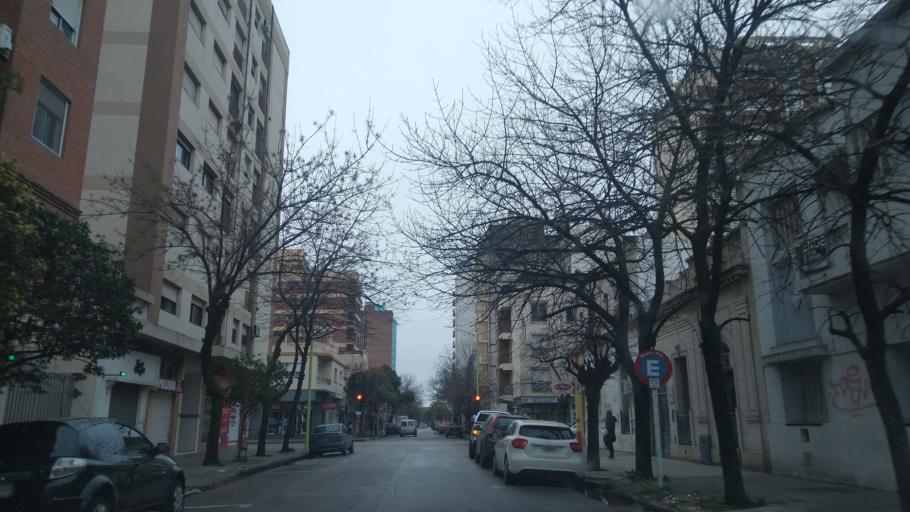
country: AR
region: Buenos Aires
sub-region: Partido de Bahia Blanca
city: Bahia Blanca
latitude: -38.7139
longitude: -62.2695
